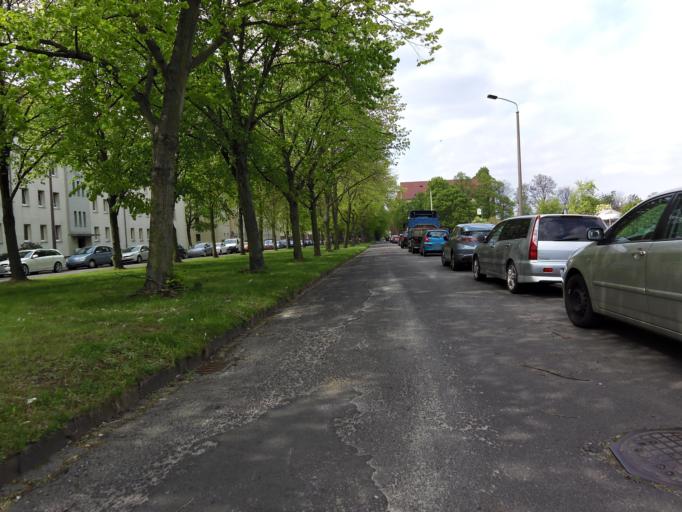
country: DE
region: Saxony
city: Leipzig
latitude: 51.3686
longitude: 12.3932
